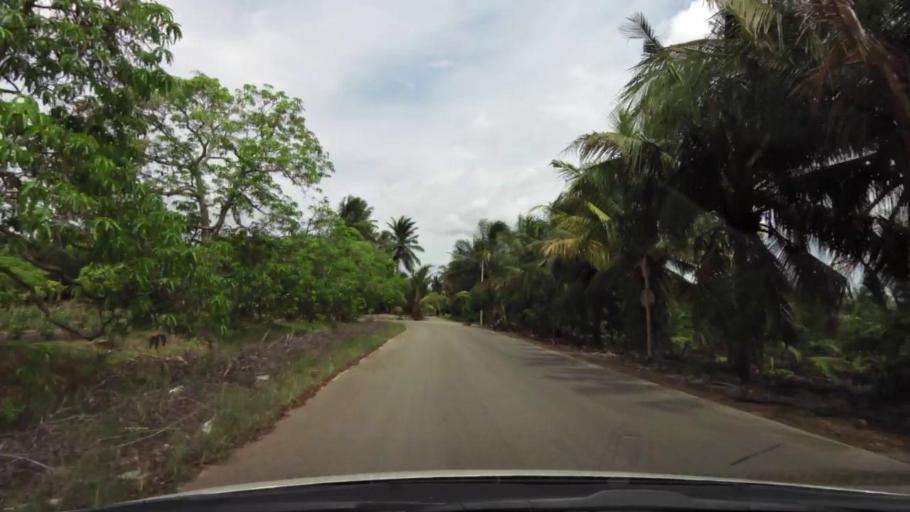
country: TH
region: Ratchaburi
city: Damnoen Saduak
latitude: 13.5146
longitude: 100.0089
